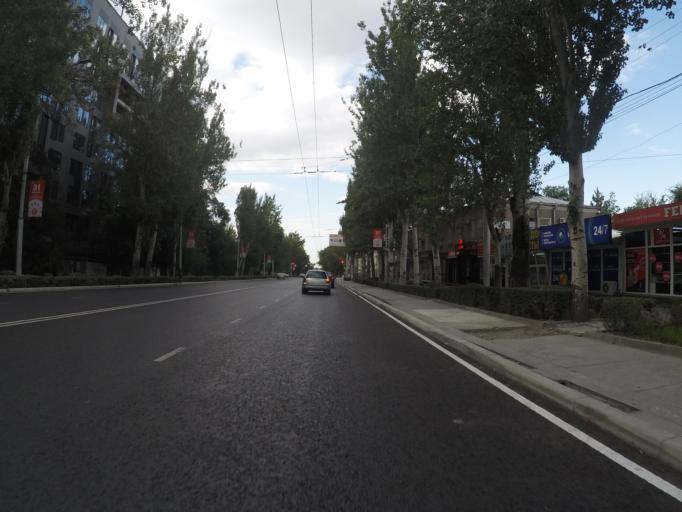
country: KG
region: Chuy
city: Bishkek
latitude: 42.8689
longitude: 74.5876
